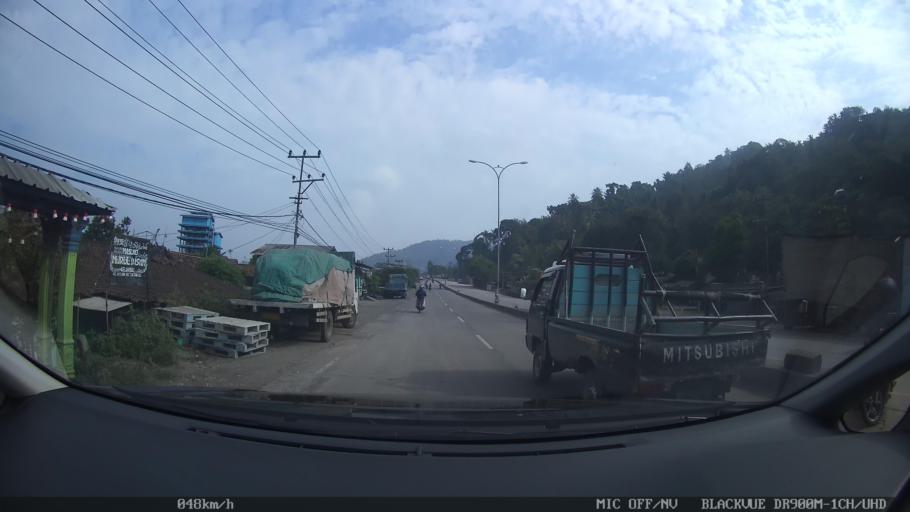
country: ID
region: Lampung
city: Panjang
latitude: -5.4566
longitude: 105.3158
